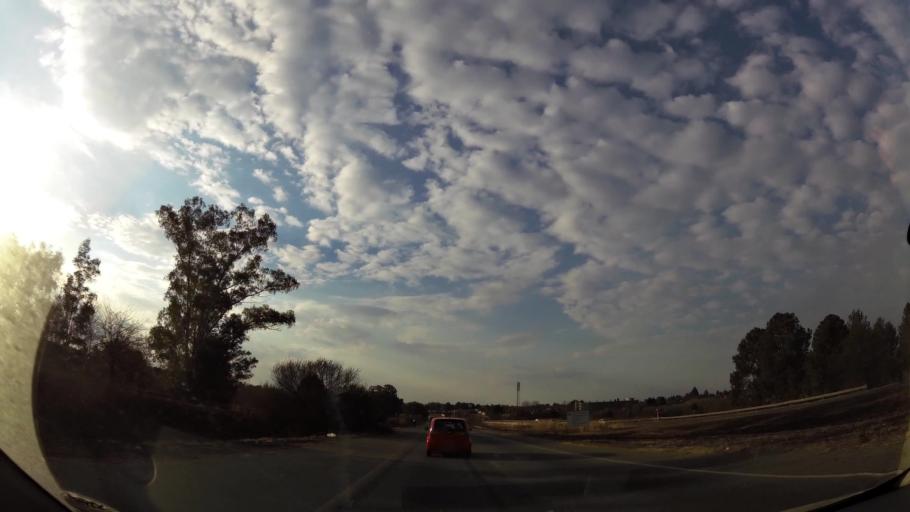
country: ZA
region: Gauteng
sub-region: Sedibeng District Municipality
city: Vanderbijlpark
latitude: -26.7542
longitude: 27.8255
